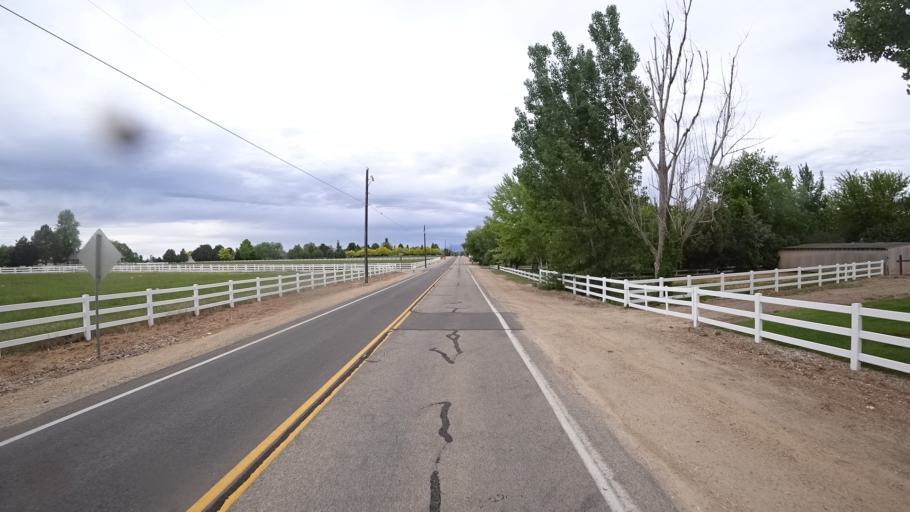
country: US
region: Idaho
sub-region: Ada County
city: Meridian
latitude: 43.5773
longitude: -116.4137
